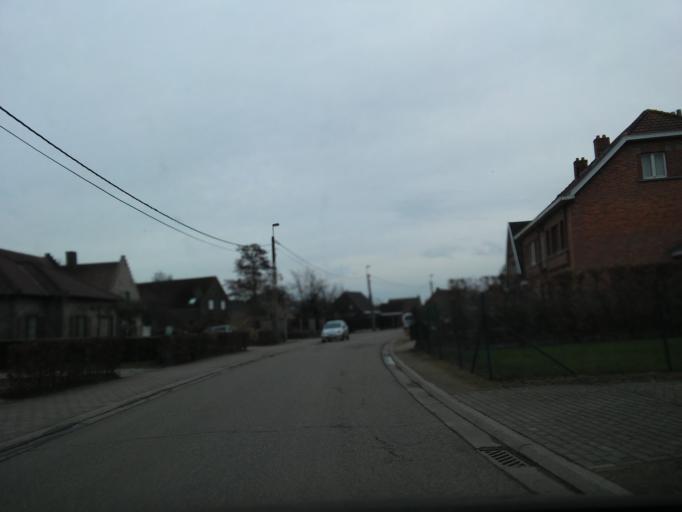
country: BE
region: Flanders
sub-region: Provincie Oost-Vlaanderen
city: Hamme
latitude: 51.1003
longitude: 4.1568
